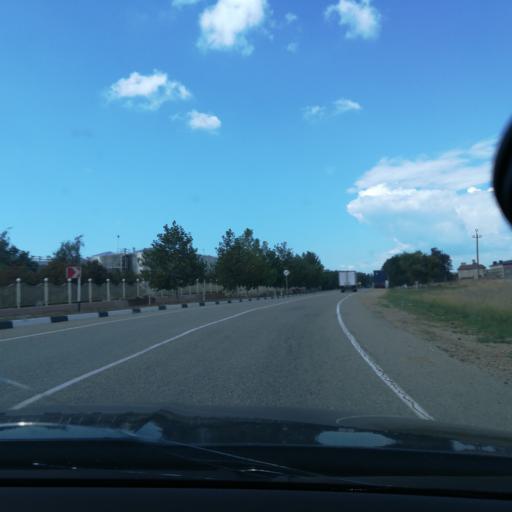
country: RU
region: Krasnodarskiy
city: Taman'
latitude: 45.2190
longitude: 36.7467
